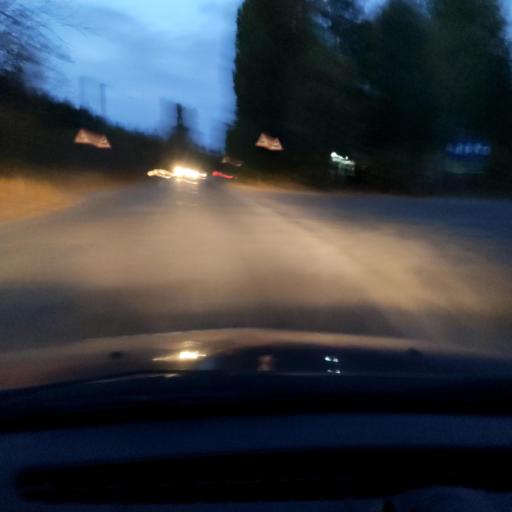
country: RU
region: Voronezj
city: Pridonskoy
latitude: 51.6750
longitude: 39.0985
